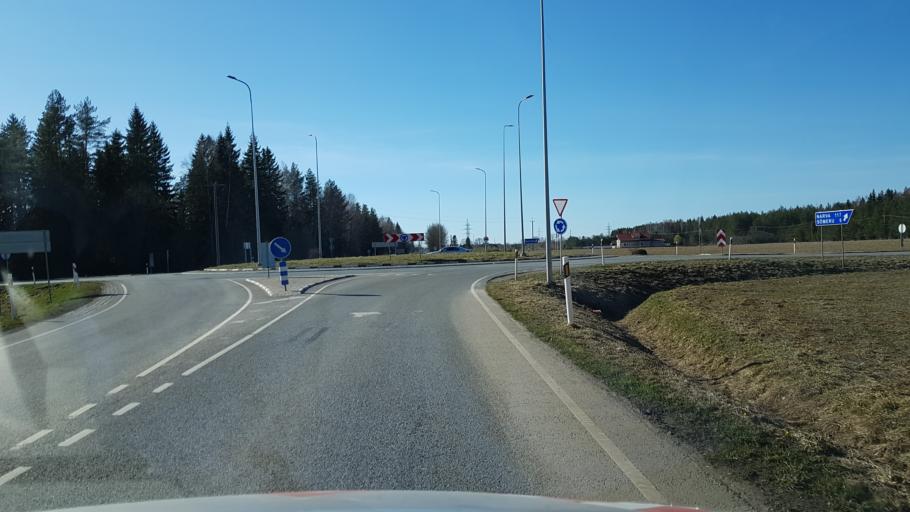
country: EE
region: Laeaene-Virumaa
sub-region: Someru vald
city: Someru
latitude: 59.3320
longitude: 26.4050
